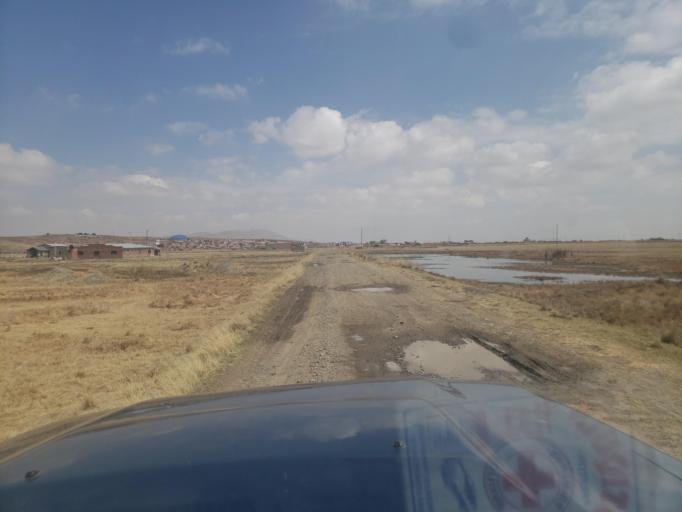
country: BO
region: La Paz
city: Batallas
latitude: -16.4036
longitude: -68.4626
